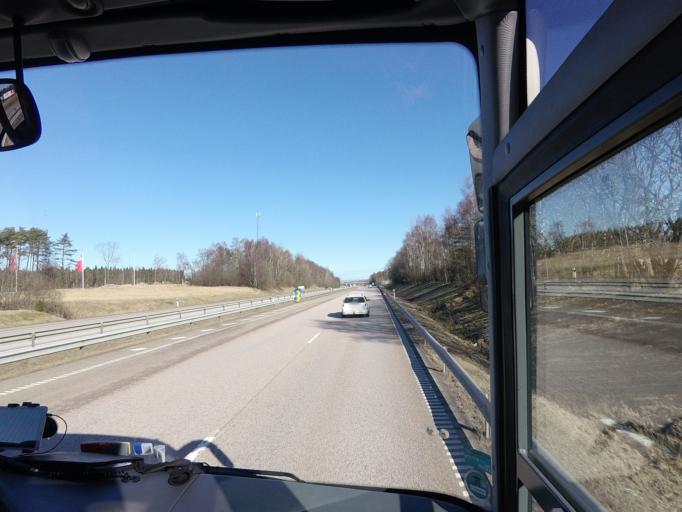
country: SE
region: Skane
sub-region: Bastads Kommun
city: Bastad
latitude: 56.3888
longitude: 12.9389
